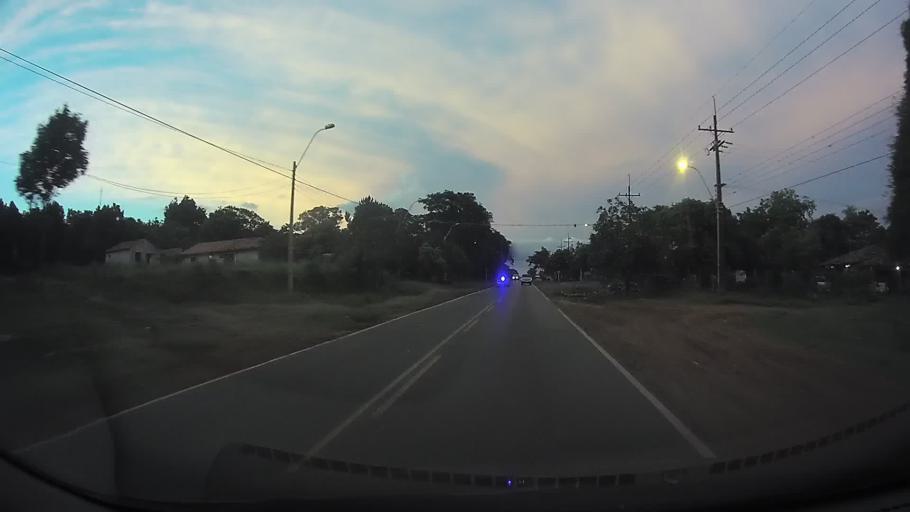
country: PY
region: Central
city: Ita
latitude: -25.4626
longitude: -57.3660
